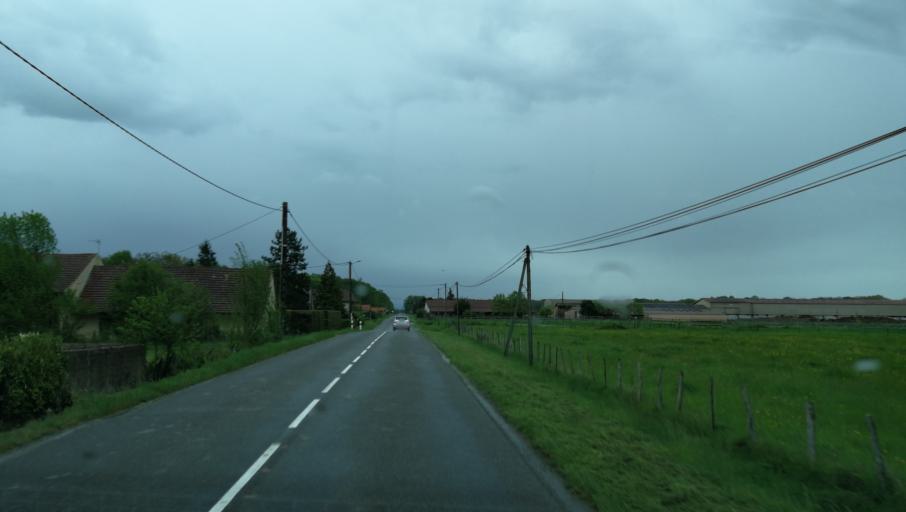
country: FR
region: Bourgogne
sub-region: Departement de Saone-et-Loire
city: Pierre-de-Bresse
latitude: 46.8760
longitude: 5.2797
